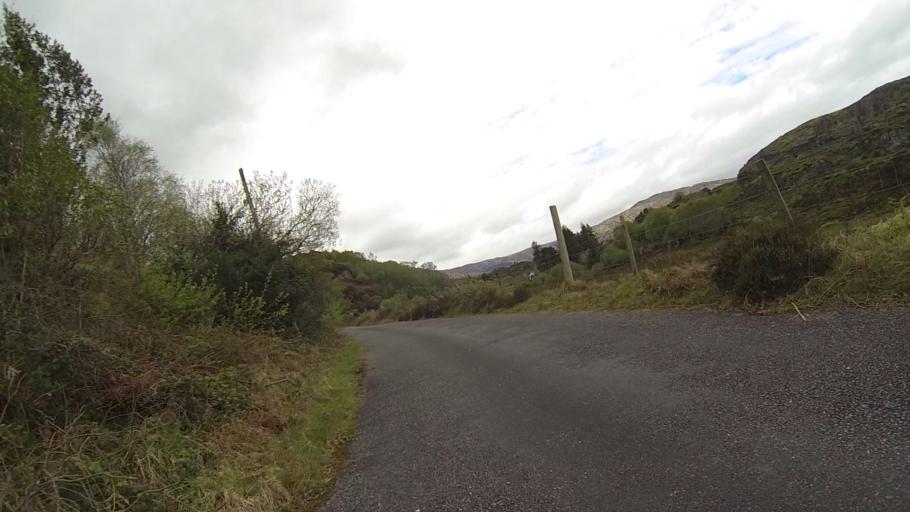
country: IE
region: Munster
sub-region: County Cork
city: Bantry
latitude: 51.7184
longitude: -9.5751
